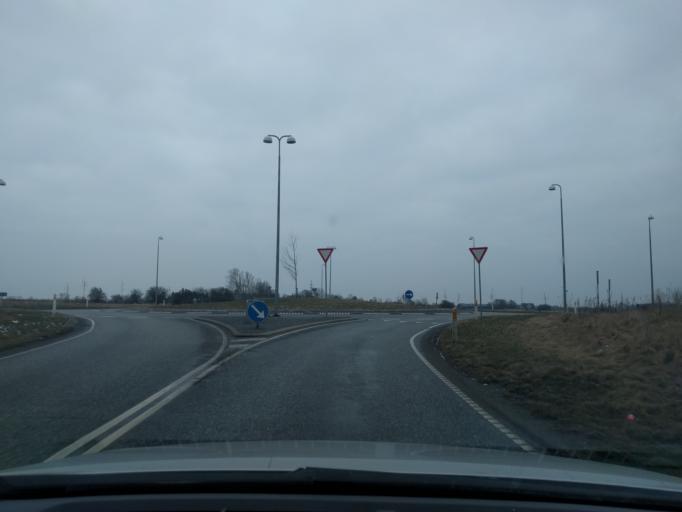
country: DK
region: South Denmark
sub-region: Middelfart Kommune
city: Strib
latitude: 55.4930
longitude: 9.8142
